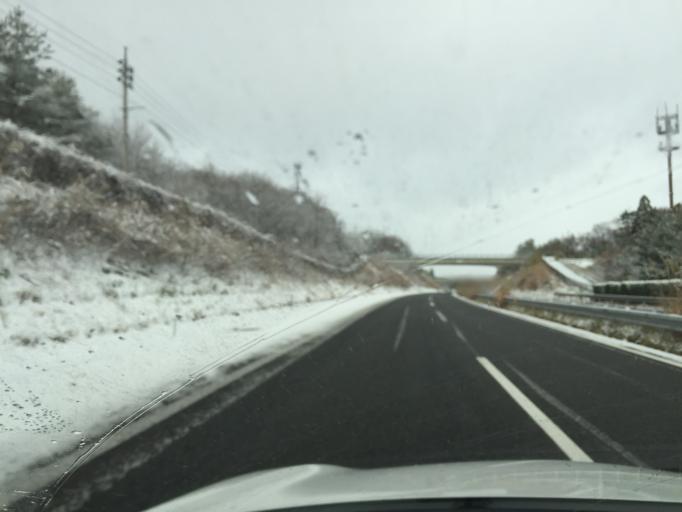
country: JP
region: Fukushima
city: Koriyama
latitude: 37.4454
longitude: 140.4165
